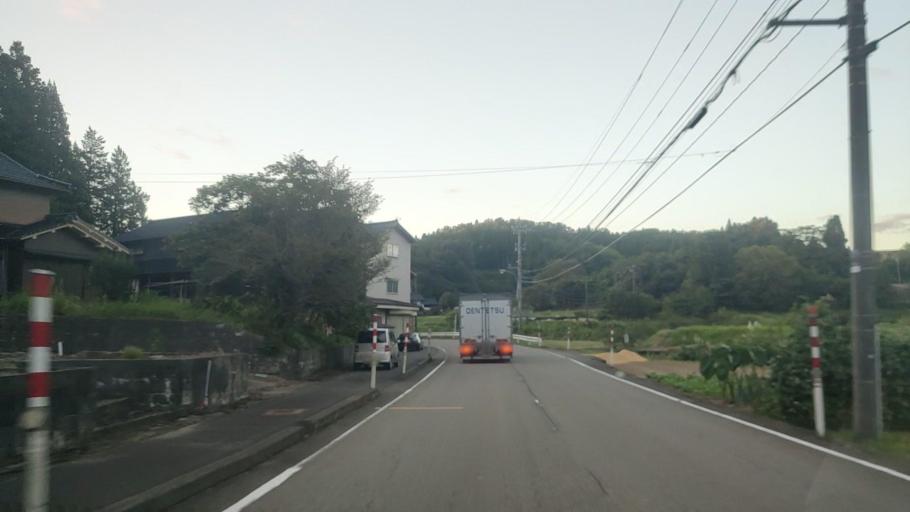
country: JP
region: Ishikawa
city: Tsubata
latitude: 36.6429
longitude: 136.7669
